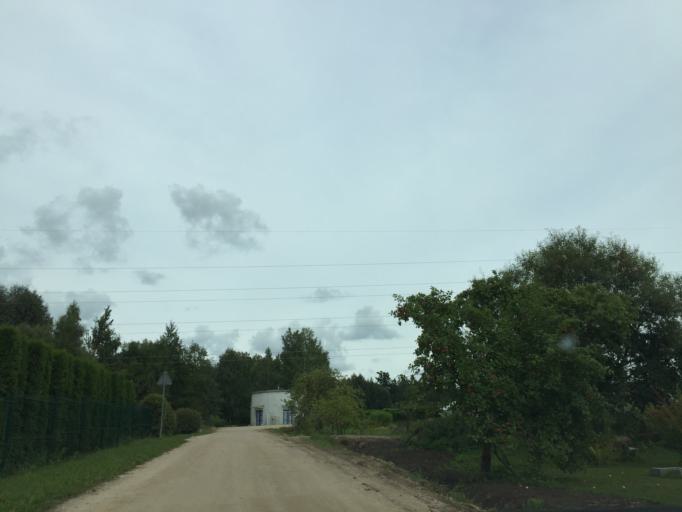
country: LV
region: Kegums
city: Kegums
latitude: 56.7466
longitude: 24.7081
